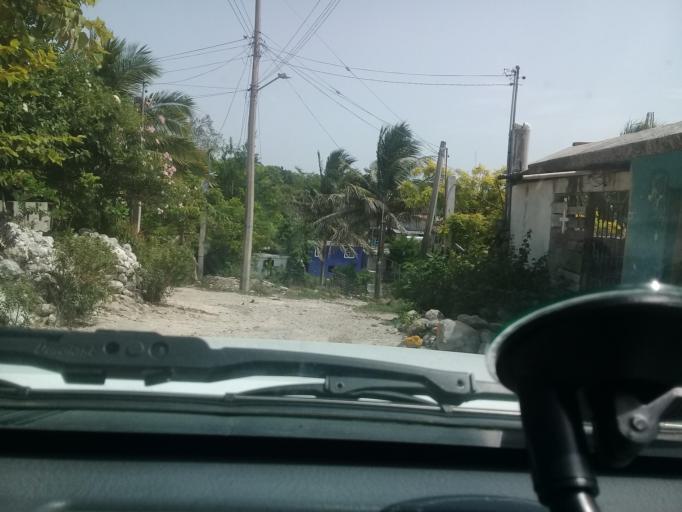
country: MX
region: Veracruz
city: Anahuac
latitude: 22.2135
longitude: -97.8345
